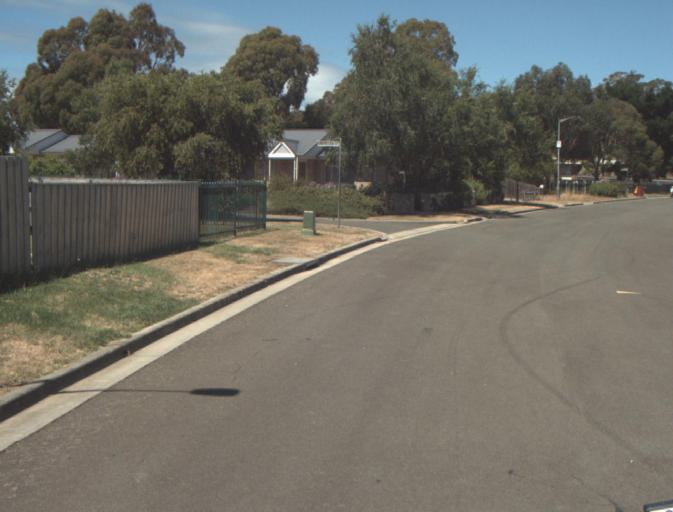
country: AU
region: Tasmania
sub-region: Launceston
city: Mayfield
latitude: -41.3757
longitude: 147.1380
